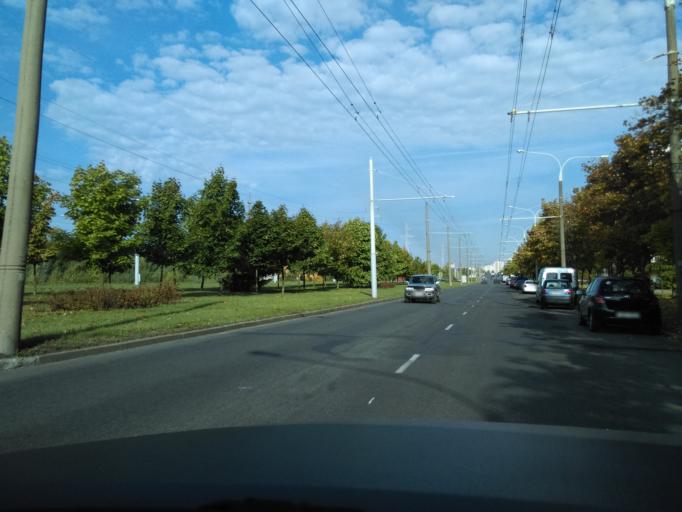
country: BY
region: Minsk
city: Minsk
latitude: 53.8538
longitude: 27.5949
